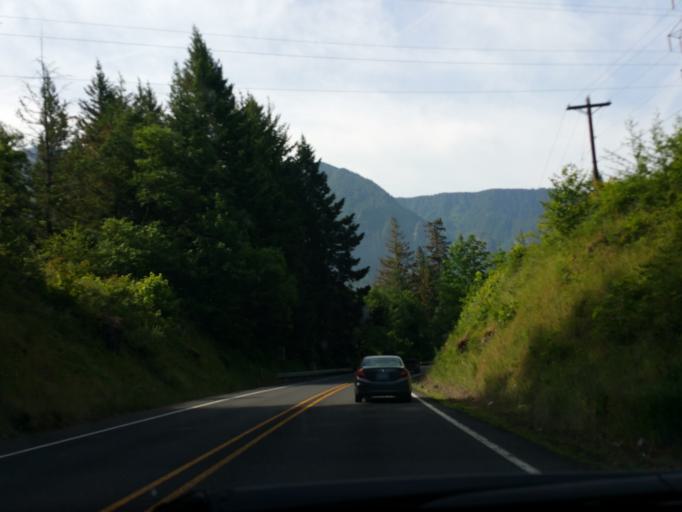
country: US
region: Oregon
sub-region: Hood River County
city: Cascade Locks
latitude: 45.6249
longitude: -122.0248
